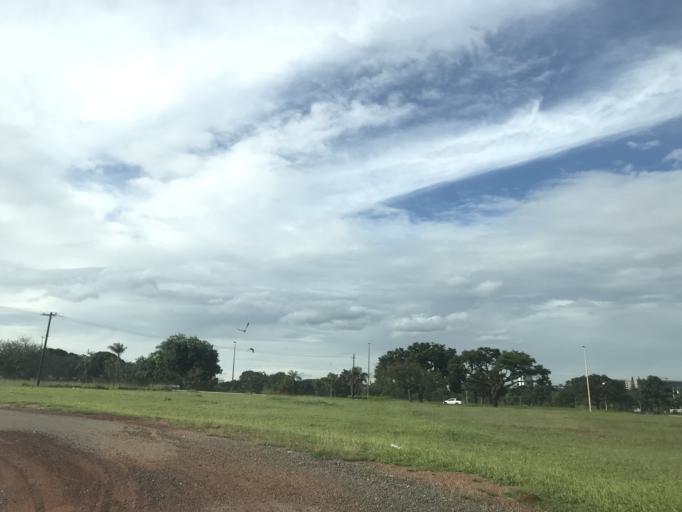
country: BR
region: Federal District
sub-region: Brasilia
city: Brasilia
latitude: -15.8128
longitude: -47.8829
